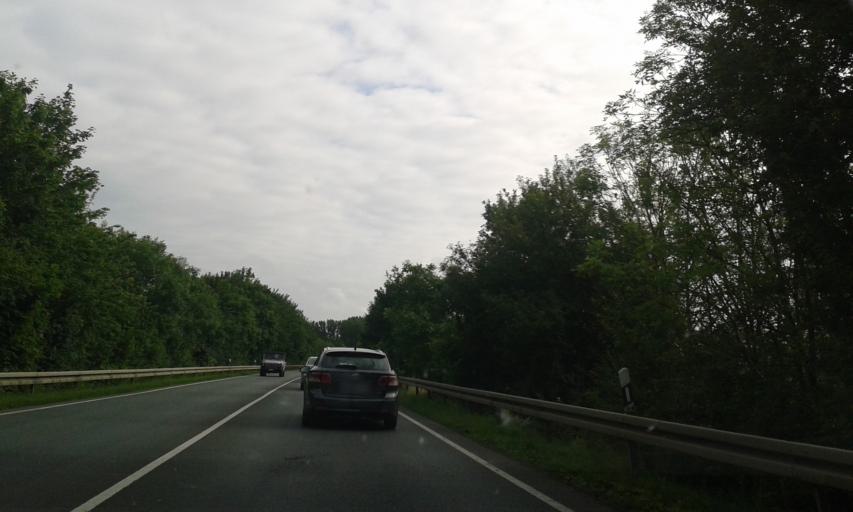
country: DE
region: Lower Saxony
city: Rinteln
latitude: 52.1819
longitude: 9.0947
